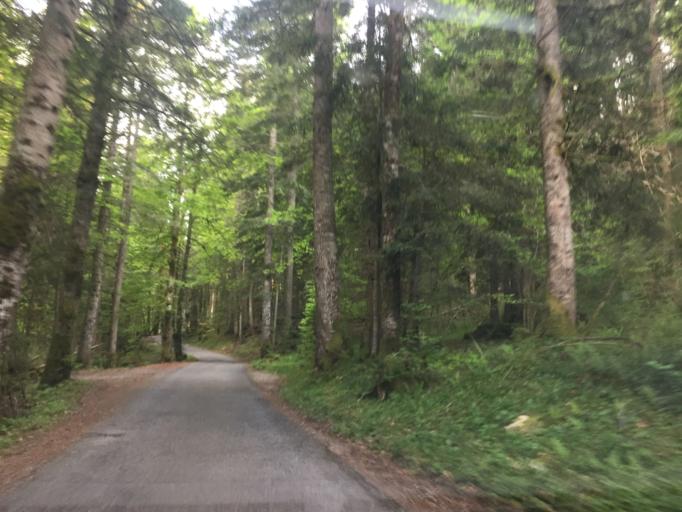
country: FR
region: Rhone-Alpes
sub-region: Departement de l'Isere
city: Le Sappey-en-Chartreuse
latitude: 45.3031
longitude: 5.8104
